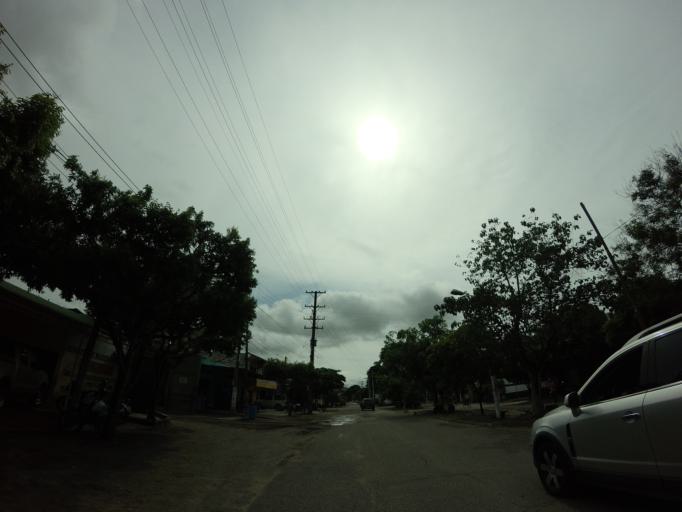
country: CO
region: Caldas
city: La Dorada
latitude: 5.4468
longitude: -74.6671
